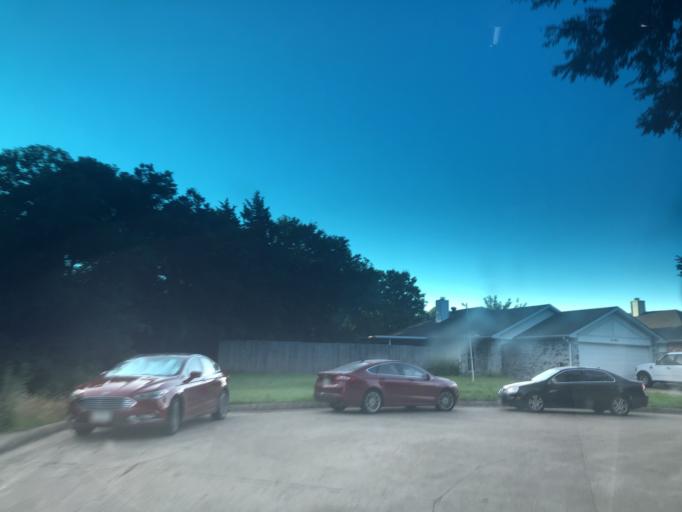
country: US
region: Texas
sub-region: Dallas County
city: Grand Prairie
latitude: 32.6938
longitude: -97.0165
